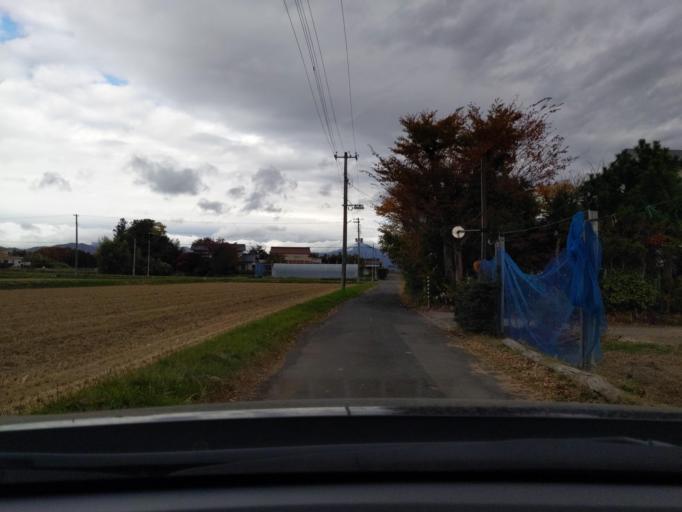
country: JP
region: Fukushima
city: Koriyama
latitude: 37.4092
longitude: 140.3036
